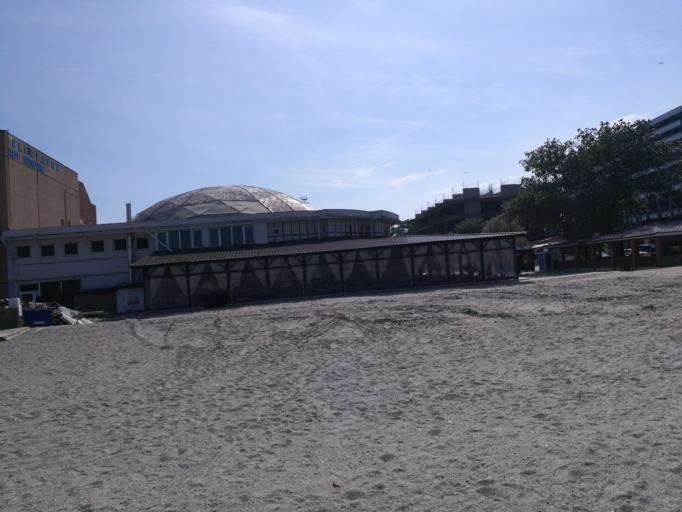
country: RO
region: Constanta
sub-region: Municipiul Constanta
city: Palazu Mare
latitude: 44.2232
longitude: 28.6337
